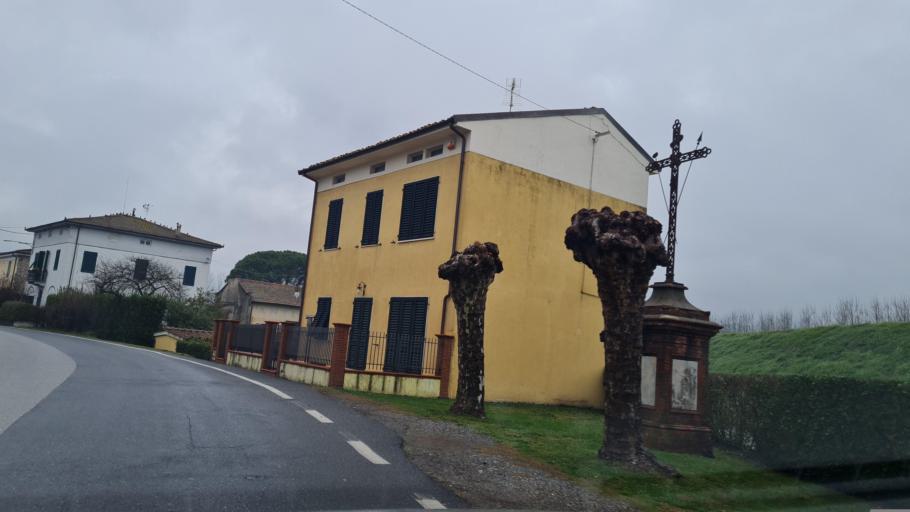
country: IT
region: Tuscany
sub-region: Provincia di Lucca
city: Lucca
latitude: 43.8562
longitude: 10.4462
